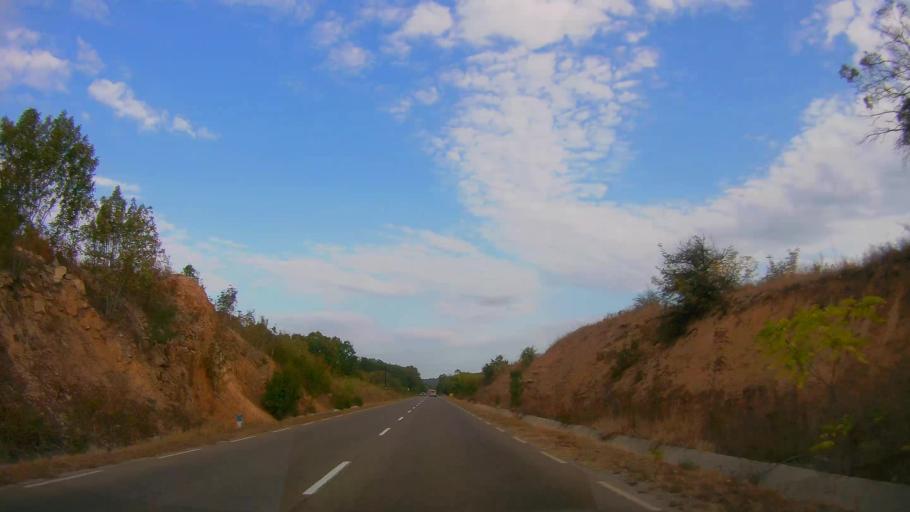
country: BG
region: Burgas
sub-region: Obshtina Sozopol
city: Sozopol
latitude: 42.3498
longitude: 27.7117
